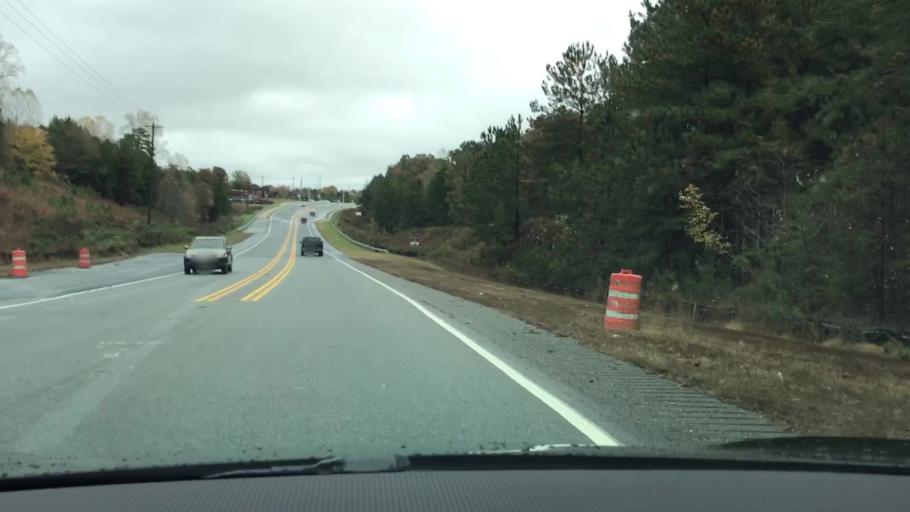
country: US
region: Georgia
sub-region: Gwinnett County
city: Buford
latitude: 34.1504
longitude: -83.9793
